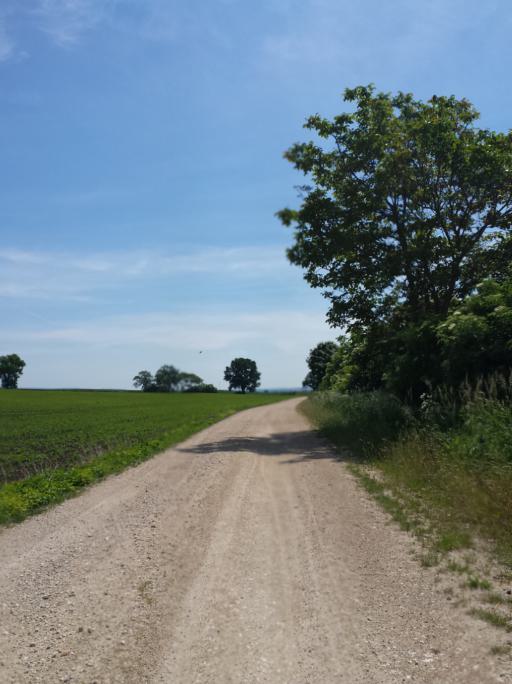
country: CZ
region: South Moravian
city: Jaroslavice
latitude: 48.7306
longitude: 16.2692
